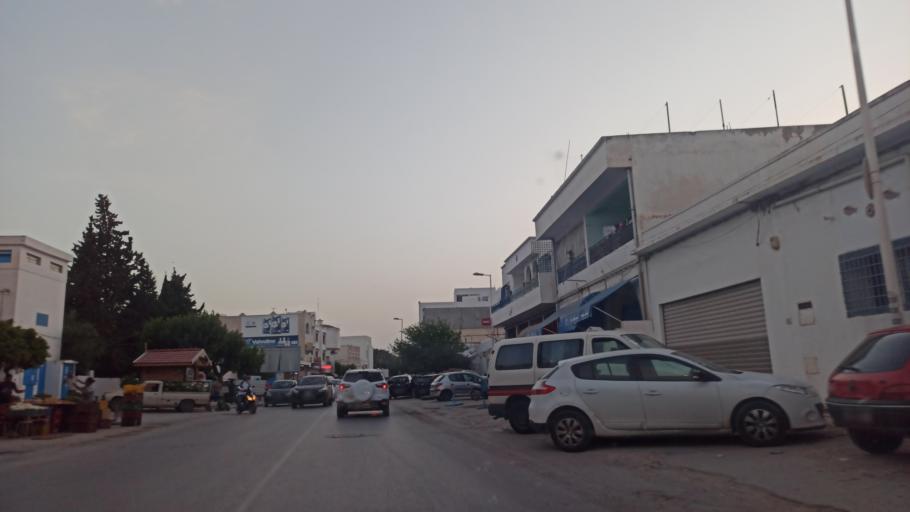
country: TN
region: Nabul
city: Al Hammamat
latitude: 36.4063
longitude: 10.6187
